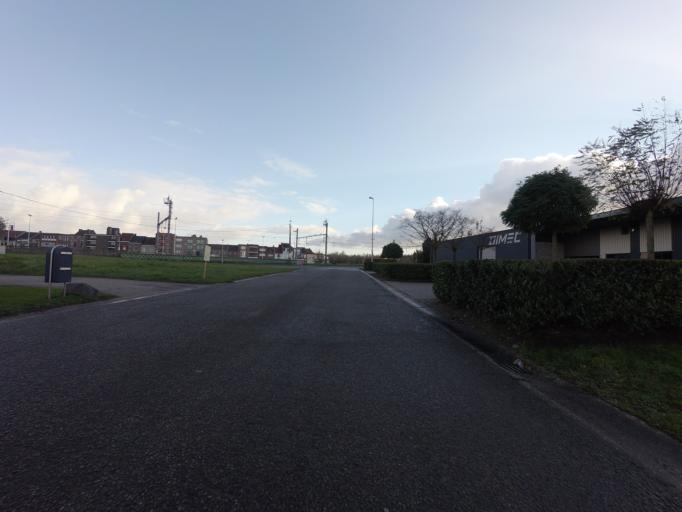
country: BE
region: Flanders
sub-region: Provincie Antwerpen
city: Boom
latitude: 51.0966
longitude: 4.3650
